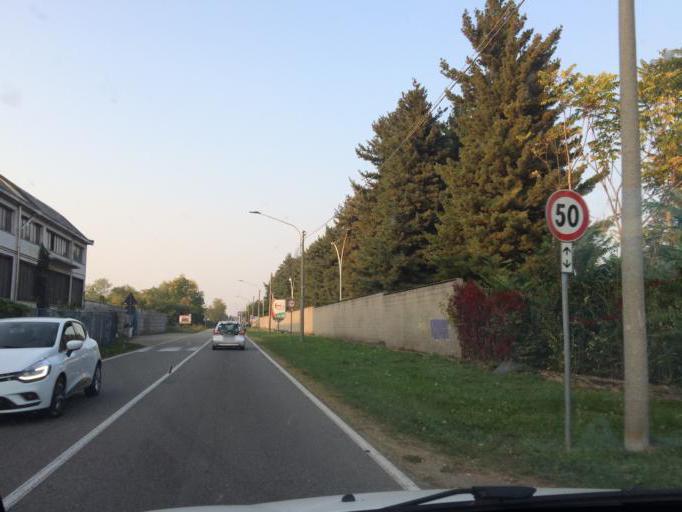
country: IT
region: Lombardy
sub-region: Provincia di Varese
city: Castellanza
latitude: 45.6179
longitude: 8.8884
